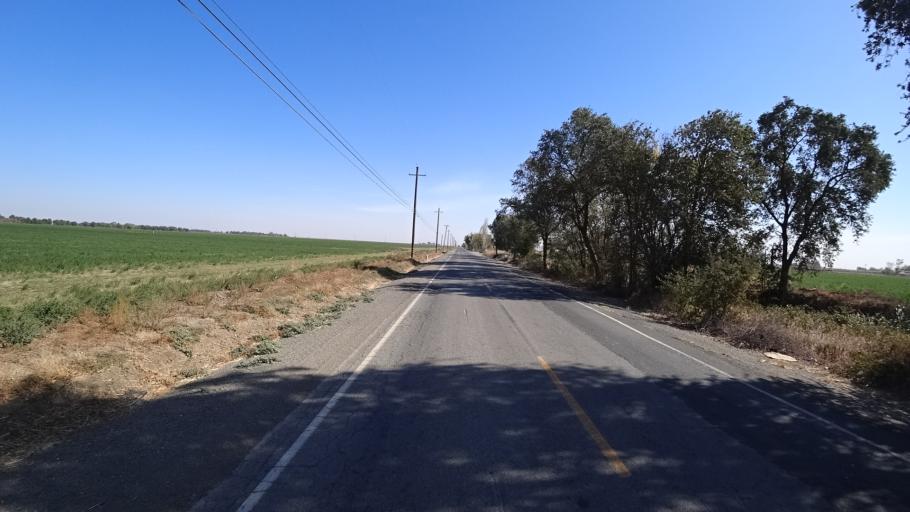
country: US
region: California
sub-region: Yolo County
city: Woodland
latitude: 38.6190
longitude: -121.7411
